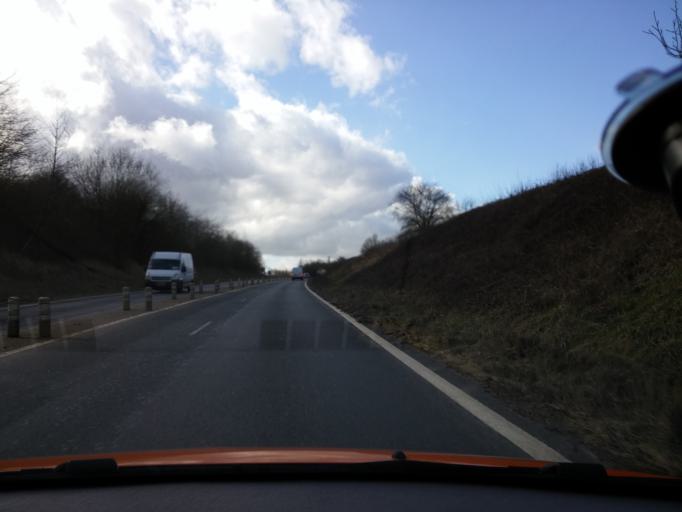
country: FR
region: Ile-de-France
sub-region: Departement de l'Essonne
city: Villebon-sur-Yvette
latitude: 48.7207
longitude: 2.2287
